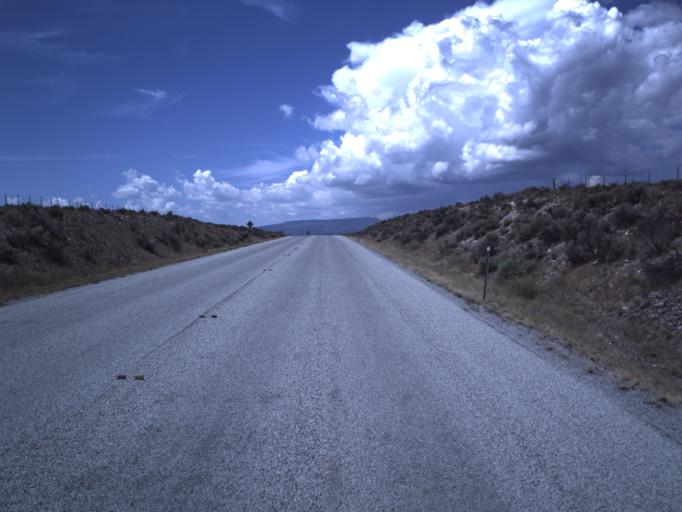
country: US
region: Utah
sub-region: Garfield County
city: Panguitch
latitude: 38.0197
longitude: -112.3661
